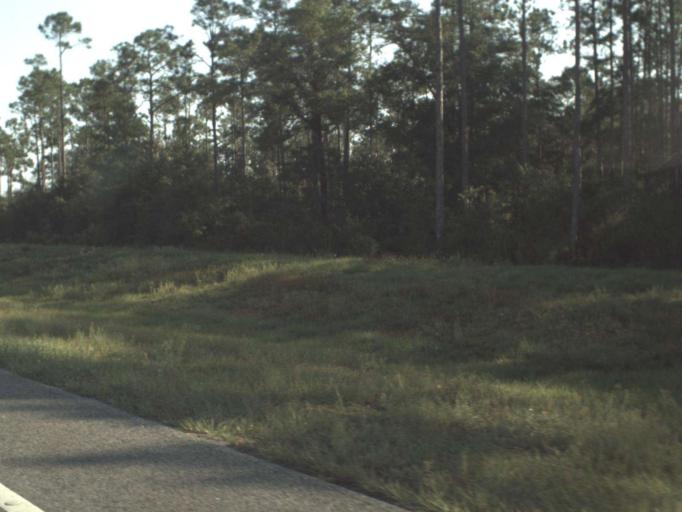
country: US
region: Florida
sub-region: Bay County
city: Laguna Beach
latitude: 30.4302
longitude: -85.8745
